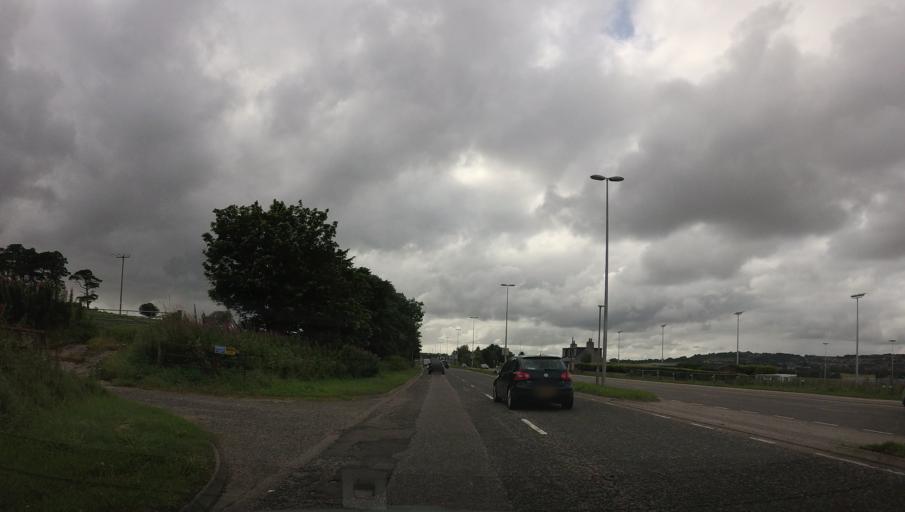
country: GB
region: Scotland
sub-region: Aberdeenshire
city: Westhill
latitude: 57.1472
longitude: -2.2559
